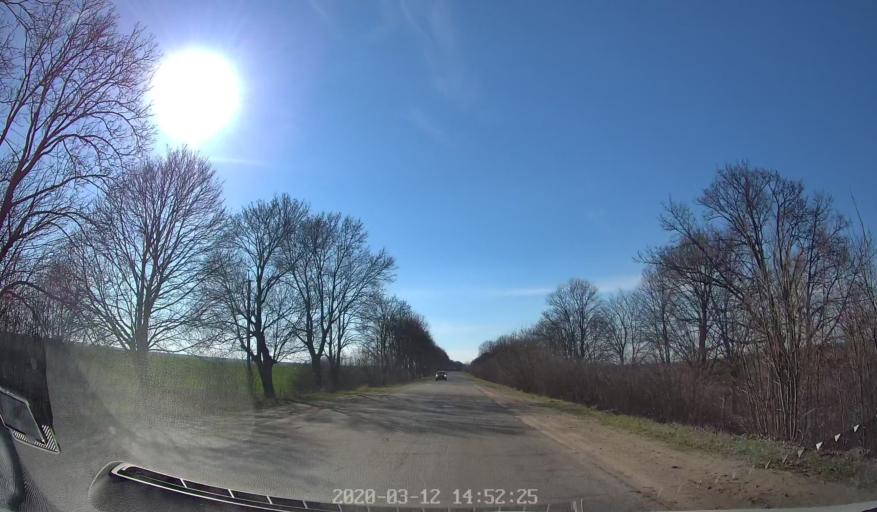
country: MD
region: Criuleni
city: Criuleni
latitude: 47.2202
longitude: 29.0991
